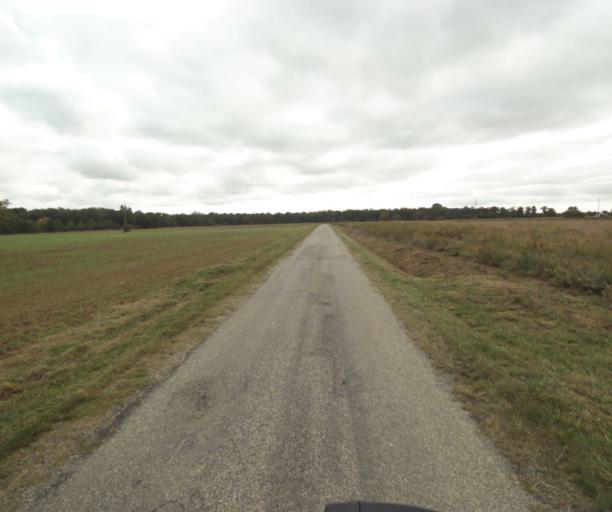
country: FR
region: Midi-Pyrenees
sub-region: Departement du Tarn-et-Garonne
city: Montech
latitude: 43.9609
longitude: 1.2547
